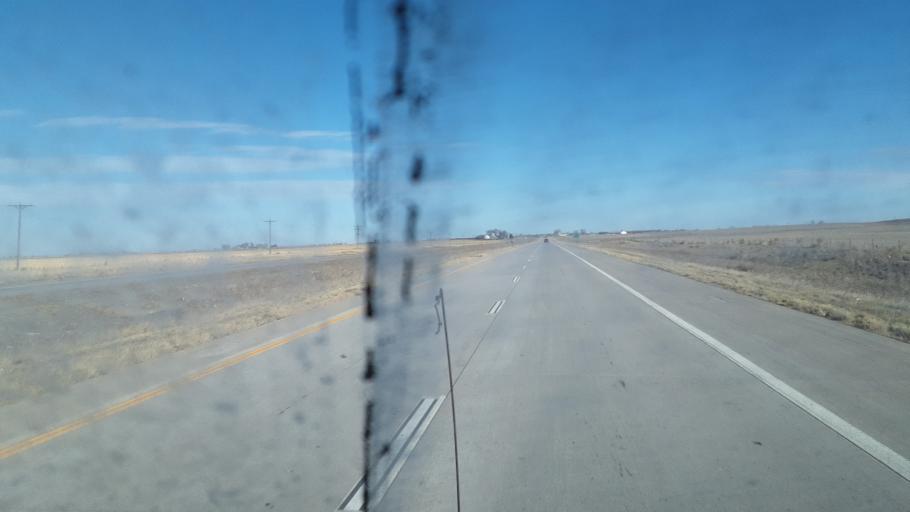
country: US
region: Colorado
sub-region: Morgan County
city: Fort Morgan
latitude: 40.2321
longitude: -104.1212
